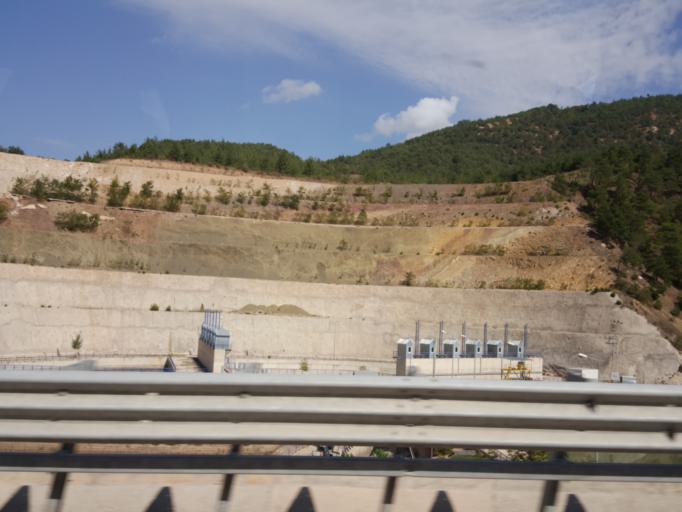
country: TR
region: Tokat
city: Basciftlik
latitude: 40.4438
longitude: 37.0796
